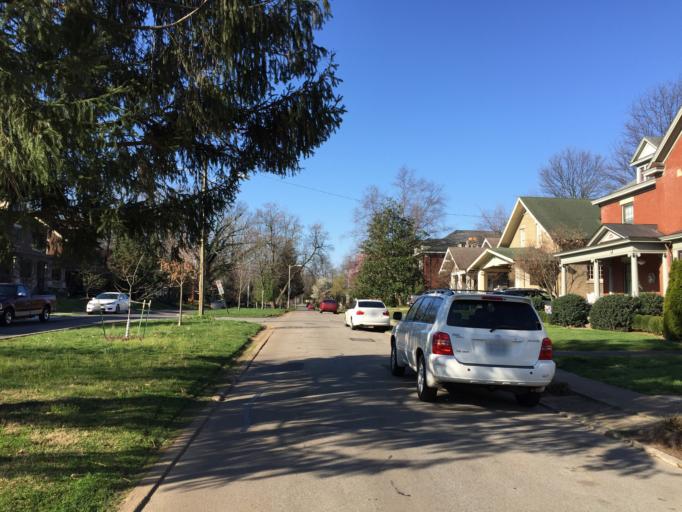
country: US
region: Kentucky
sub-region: Fayette County
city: Mount Vernon
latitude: 38.0352
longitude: -84.4801
